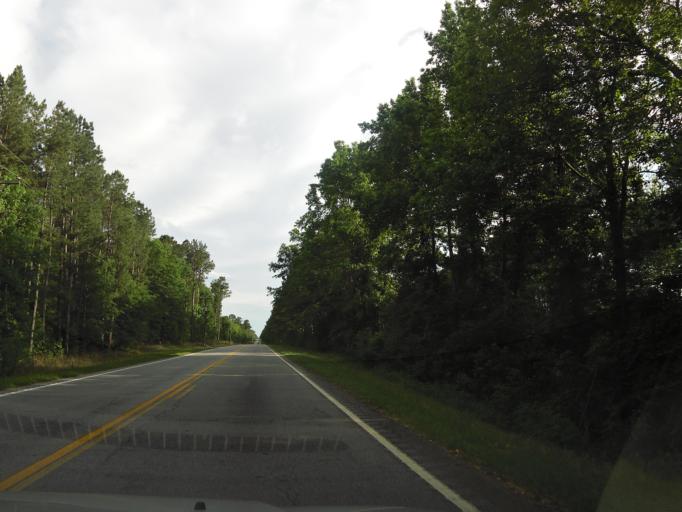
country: US
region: South Carolina
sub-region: Hampton County
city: Estill
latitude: 32.7112
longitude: -81.2424
